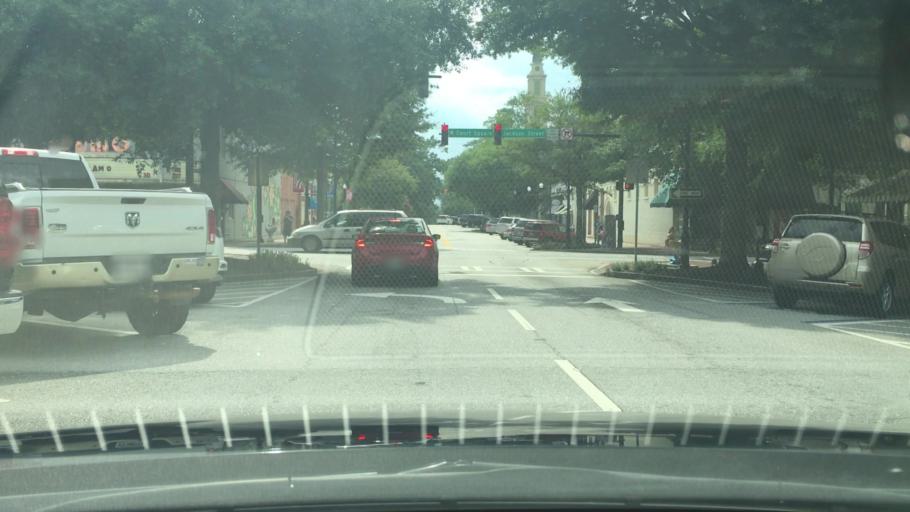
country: US
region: Georgia
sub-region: Coweta County
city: Newnan
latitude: 33.3752
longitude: -84.8000
